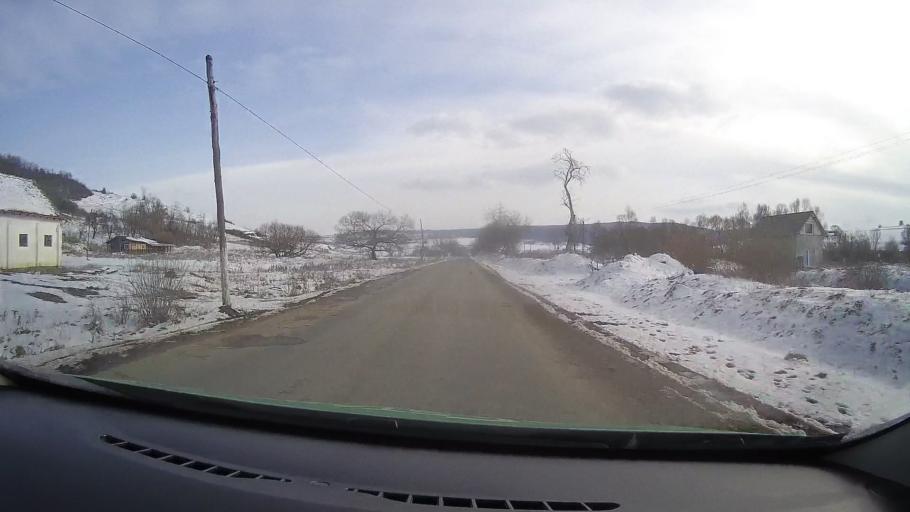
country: RO
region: Sibiu
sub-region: Comuna Iacobeni
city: Iacobeni
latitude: 46.0446
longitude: 24.7268
